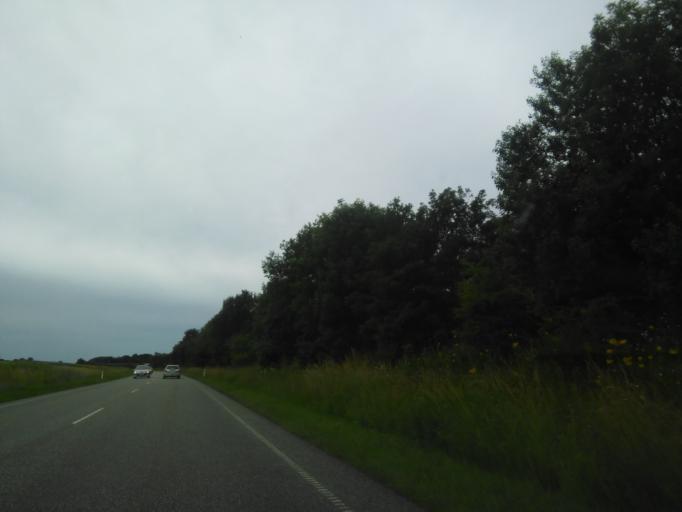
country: DK
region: Central Jutland
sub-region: Horsens Kommune
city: Horsens
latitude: 55.9116
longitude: 9.9043
